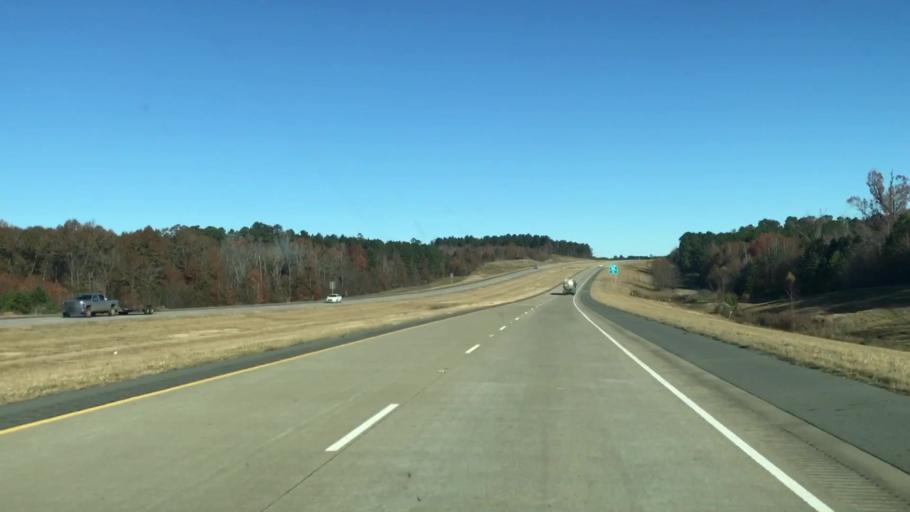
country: US
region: Louisiana
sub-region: Caddo Parish
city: Vivian
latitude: 32.9822
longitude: -93.9102
